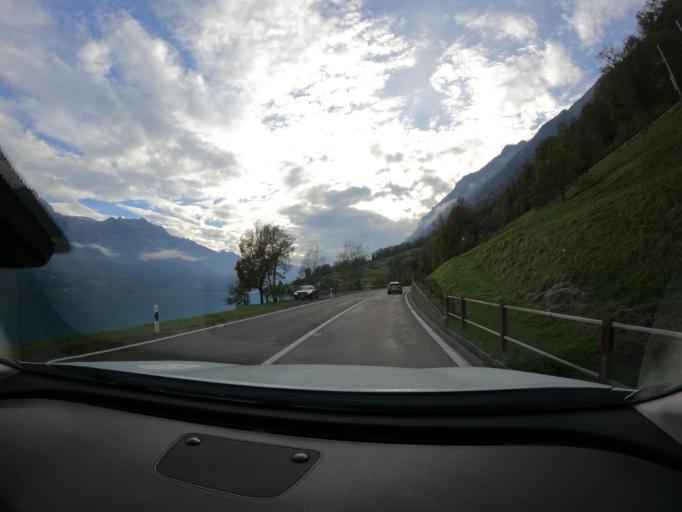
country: CH
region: Bern
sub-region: Interlaken-Oberhasli District
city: Brienz
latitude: 46.7455
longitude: 7.9771
